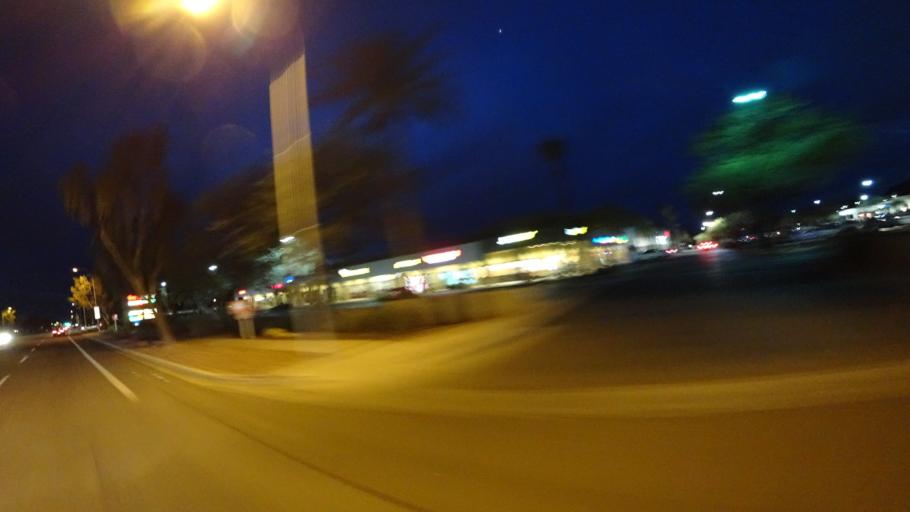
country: US
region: Arizona
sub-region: Maricopa County
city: Guadalupe
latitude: 33.3041
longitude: -111.9973
